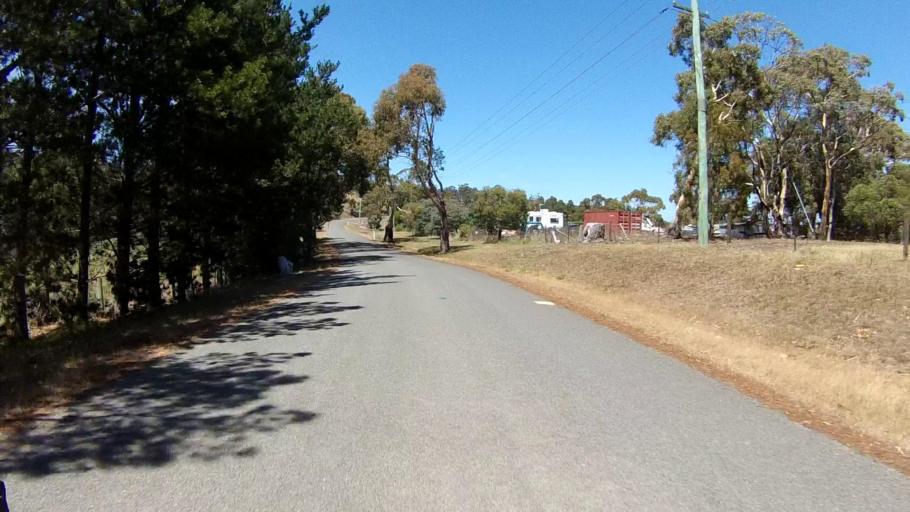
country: AU
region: Tasmania
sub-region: Clarence
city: Cambridge
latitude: -42.8474
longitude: 147.4240
